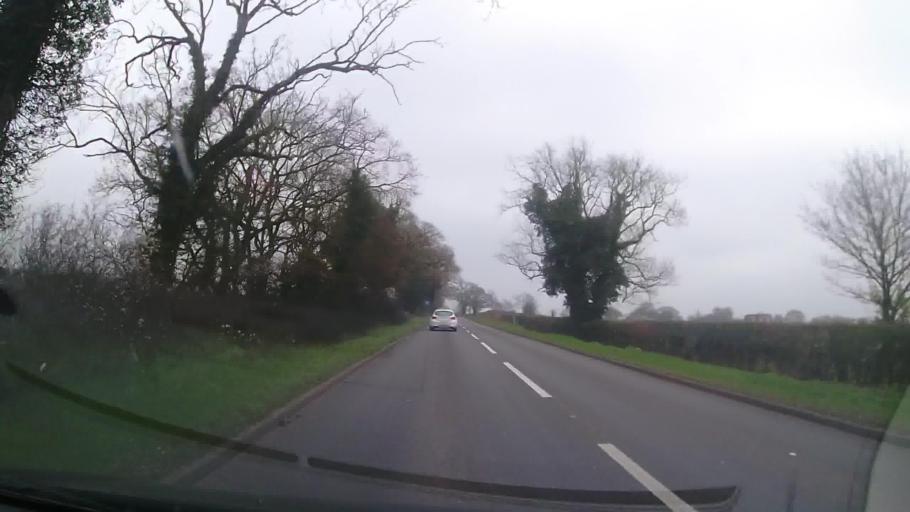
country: GB
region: England
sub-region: Shropshire
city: Market Drayton
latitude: 52.9137
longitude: -2.4390
